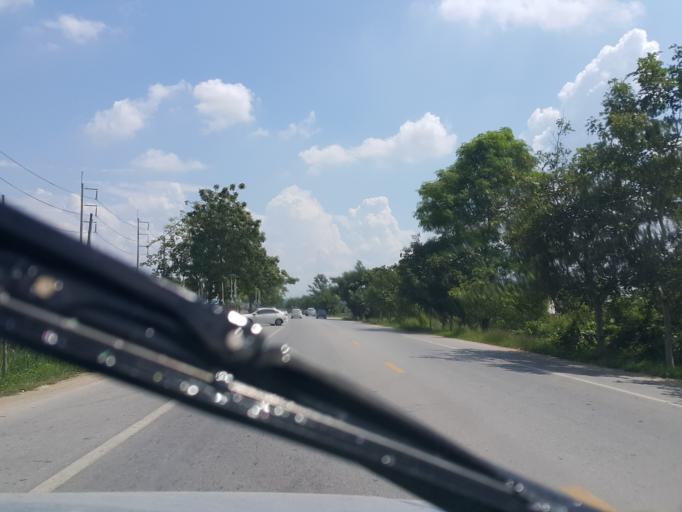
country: TH
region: Chiang Mai
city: San Sai
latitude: 18.8406
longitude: 99.0239
